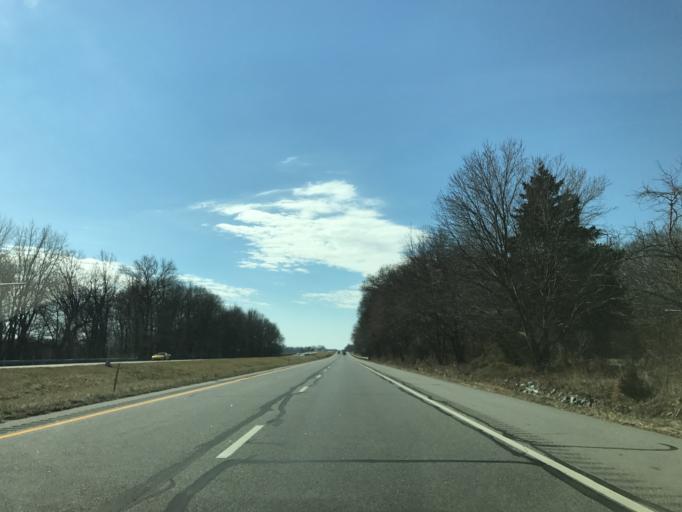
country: US
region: Delaware
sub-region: New Castle County
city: Middletown
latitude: 39.4061
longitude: -75.7762
